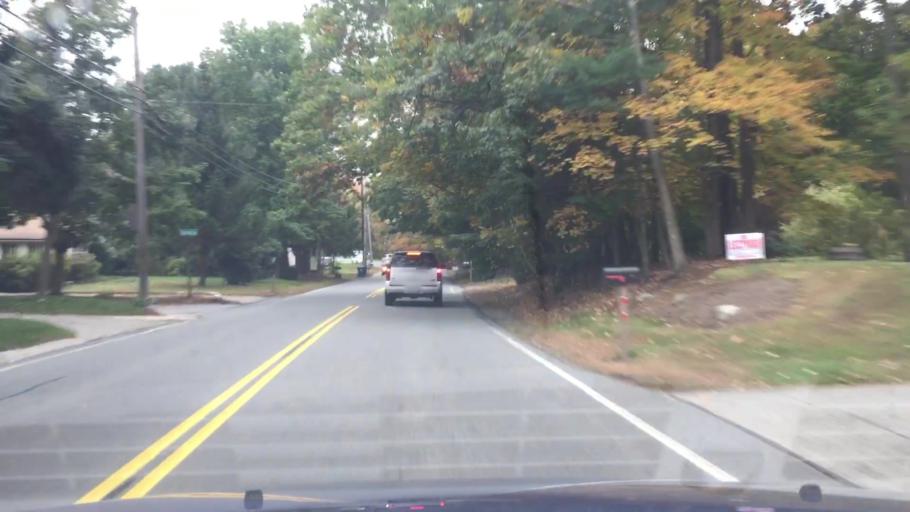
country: US
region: Massachusetts
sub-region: Middlesex County
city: Tyngsboro
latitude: 42.6947
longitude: -71.3863
